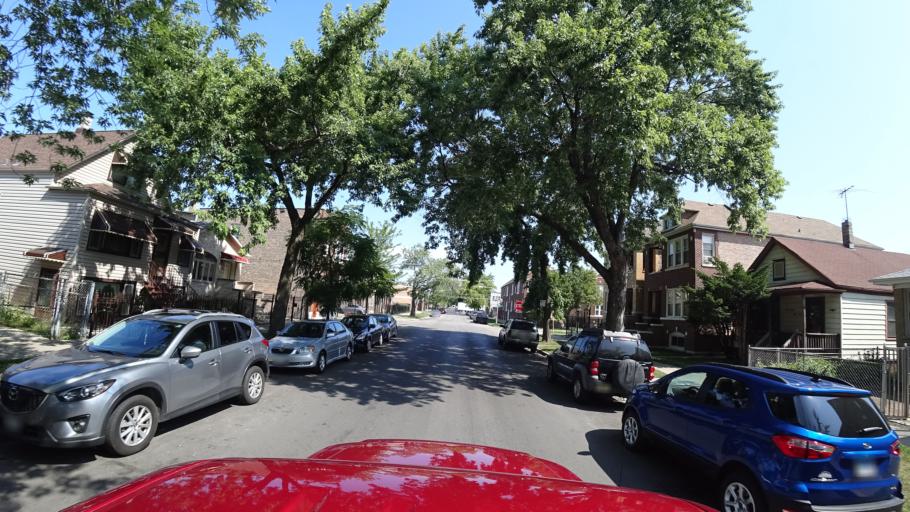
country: US
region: Illinois
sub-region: Cook County
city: Chicago
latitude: 41.8216
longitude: -87.6897
